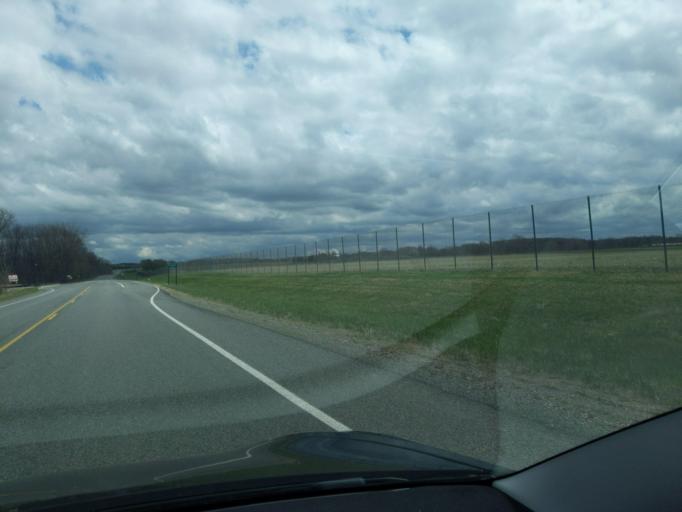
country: US
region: Michigan
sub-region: Ingham County
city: Mason
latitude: 42.5676
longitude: -84.4266
